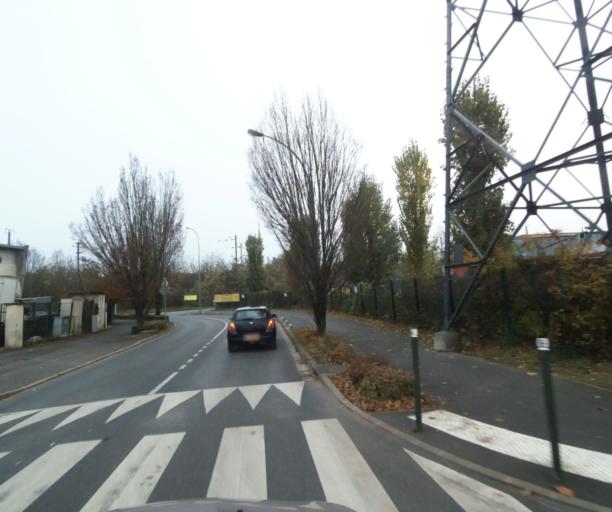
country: FR
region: Ile-de-France
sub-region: Departement de Seine-Saint-Denis
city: Gagny
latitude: 48.8736
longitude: 2.5320
